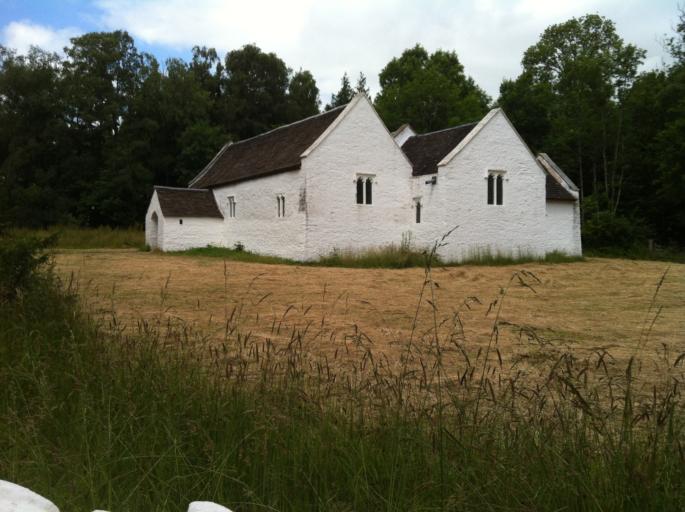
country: GB
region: Wales
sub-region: Cardiff
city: Radyr
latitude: 51.4878
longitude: -3.2798
